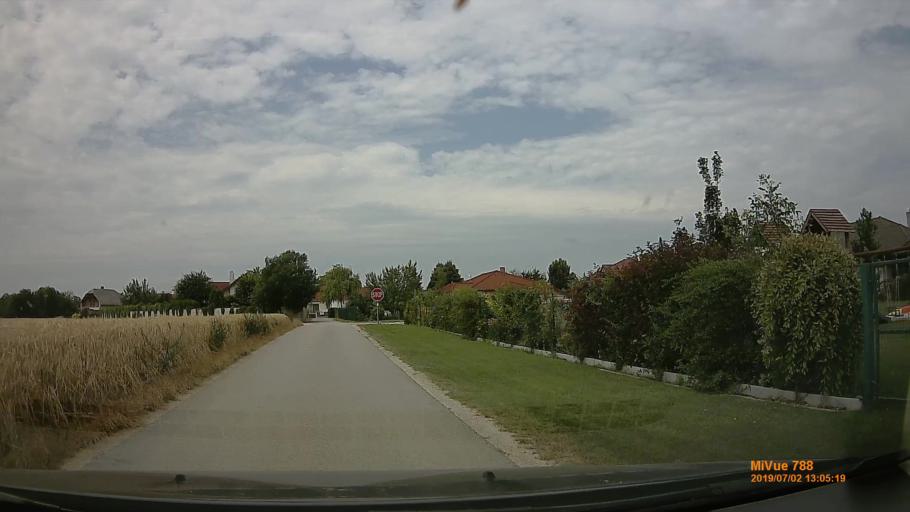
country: HU
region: Gyor-Moson-Sopron
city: Halaszi
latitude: 47.8553
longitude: 17.3245
